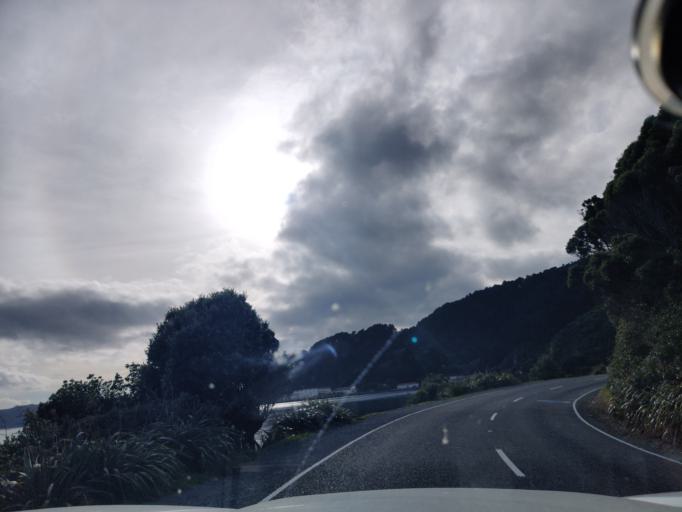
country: NZ
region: Wellington
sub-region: Wellington City
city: Wellington
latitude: -41.2993
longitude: 174.8174
